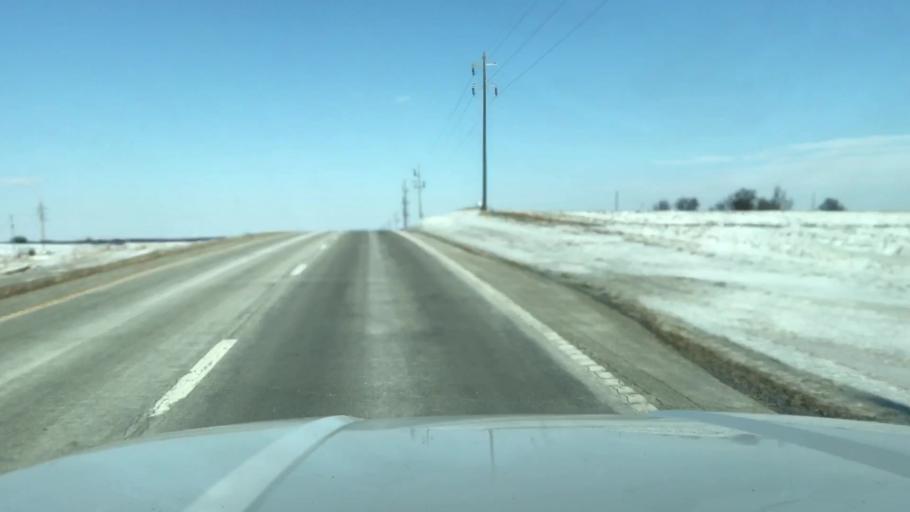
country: US
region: Missouri
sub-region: Andrew County
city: Savannah
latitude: 40.1258
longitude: -94.8695
